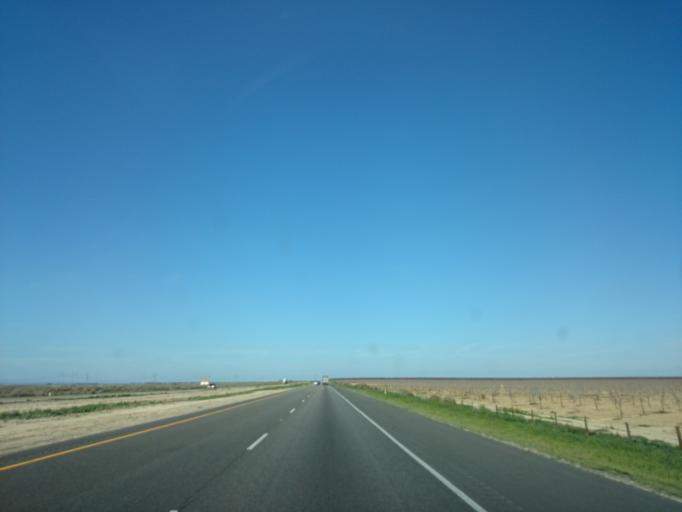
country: US
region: California
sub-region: Kern County
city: Buttonwillow
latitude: 35.4690
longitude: -119.4933
